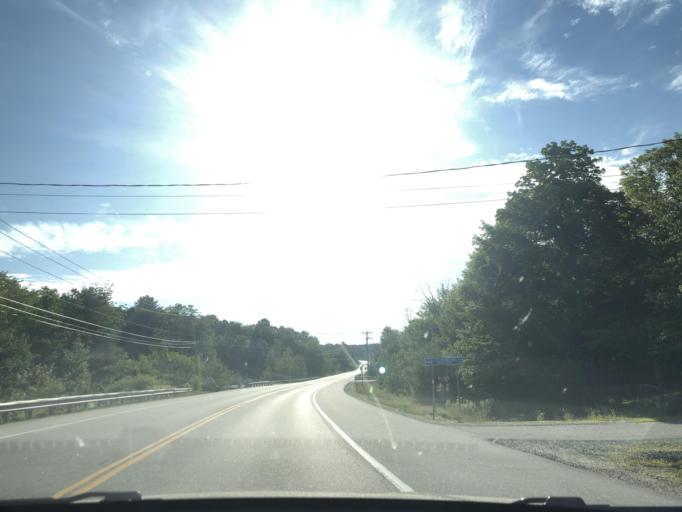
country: US
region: New Hampshire
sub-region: Merrimack County
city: New London
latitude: 43.3931
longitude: -71.9789
